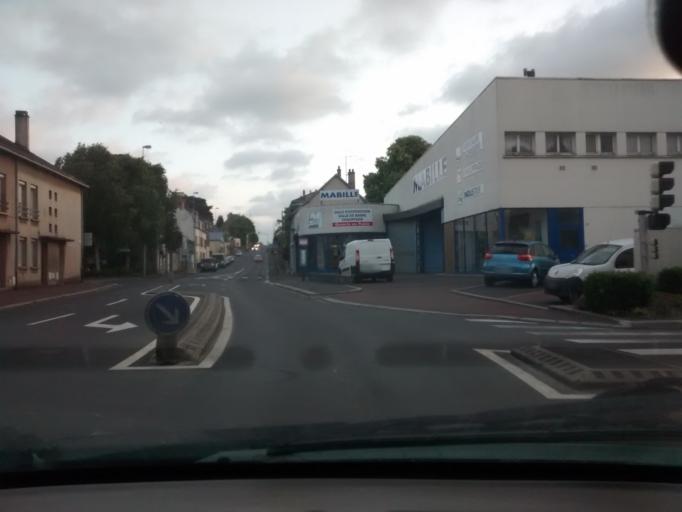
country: FR
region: Lower Normandy
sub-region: Departement de la Manche
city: Agneaux
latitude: 49.1134
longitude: -1.0997
